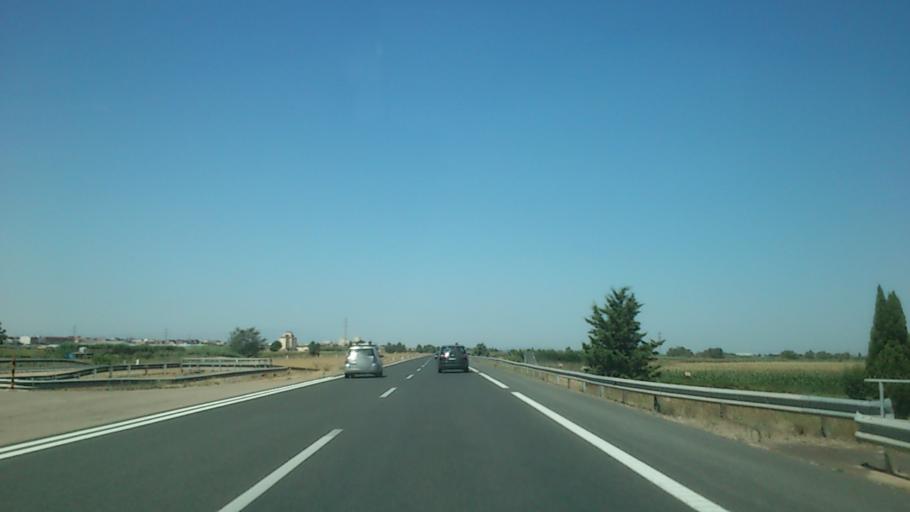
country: ES
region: Aragon
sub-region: Provincia de Zaragoza
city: Utebo
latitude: 41.7196
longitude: -0.9988
